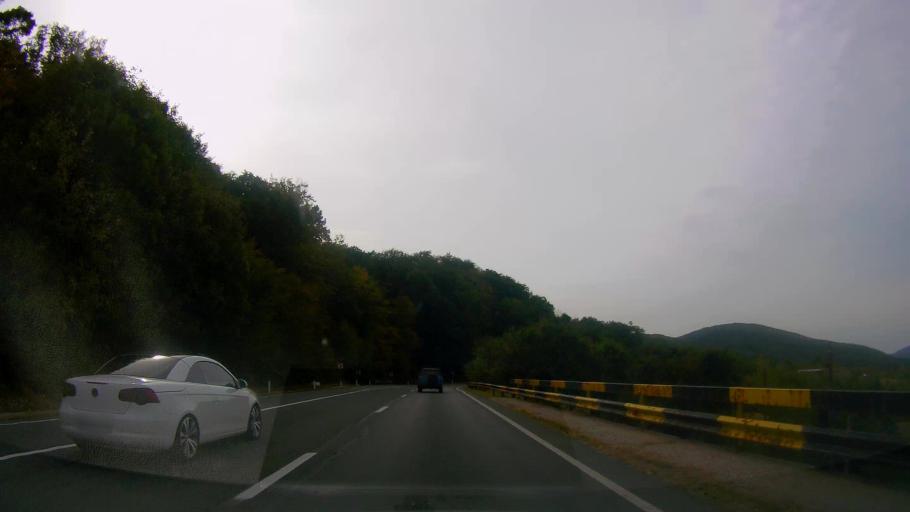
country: RO
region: Salaj
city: Zalau
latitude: 47.1589
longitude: 23.0892
